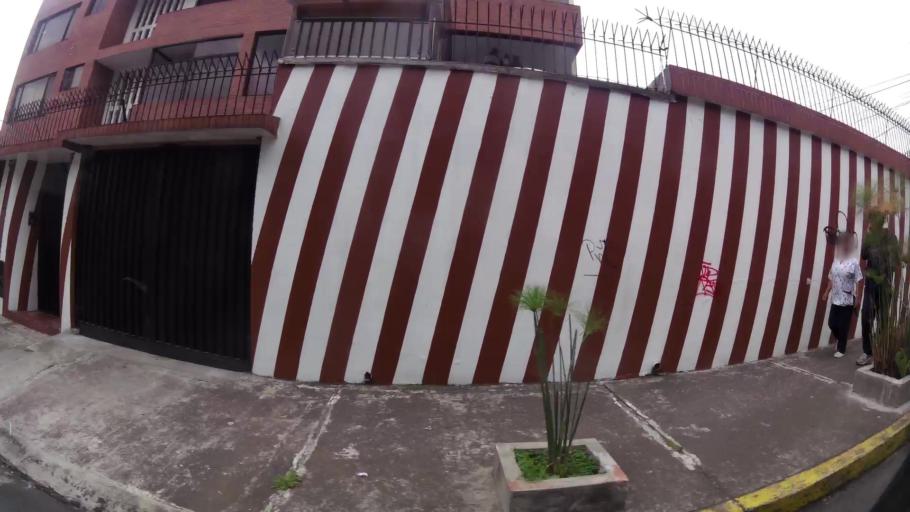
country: EC
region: Pichincha
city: Quito
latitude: -0.1581
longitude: -78.4904
